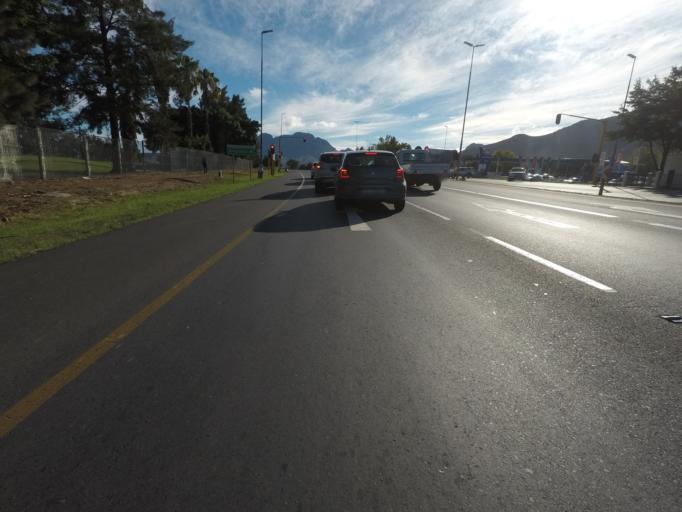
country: ZA
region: Western Cape
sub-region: Cape Winelands District Municipality
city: Stellenbosch
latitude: -33.9634
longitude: 18.8500
